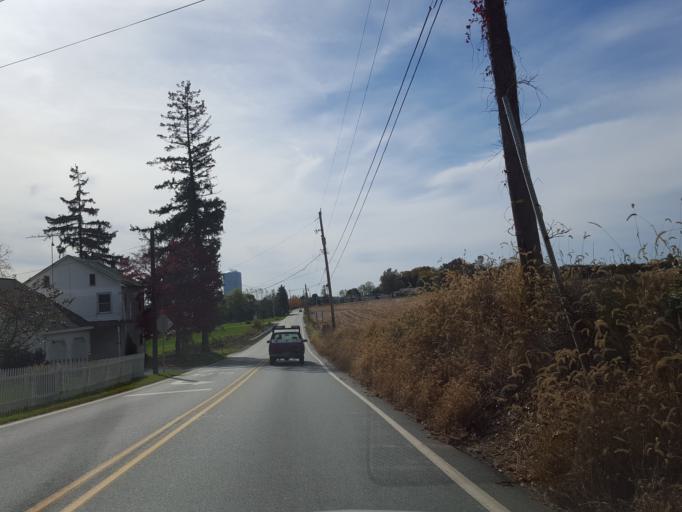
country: US
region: Pennsylvania
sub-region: York County
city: Hallam
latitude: 39.9867
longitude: -76.5699
